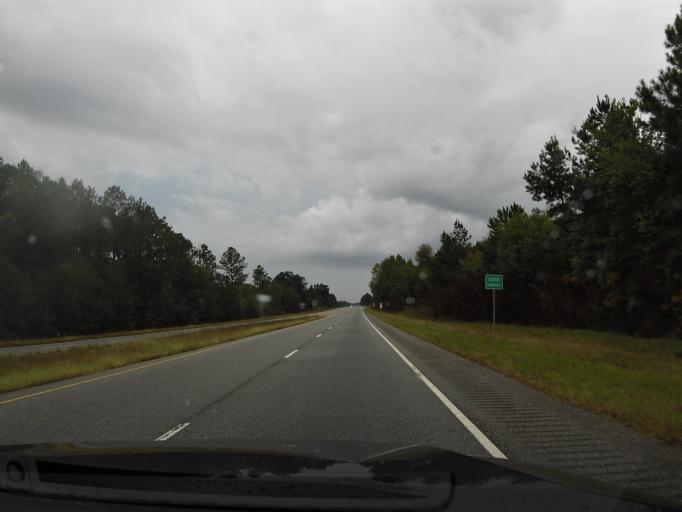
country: US
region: Georgia
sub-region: Wayne County
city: Jesup
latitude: 31.5346
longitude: -81.7943
